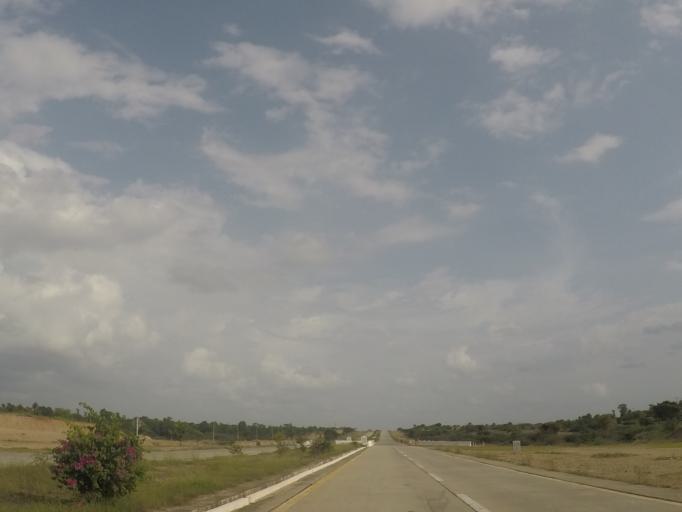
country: MM
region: Mandalay
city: Meiktila
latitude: 20.7339
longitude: 95.7780
